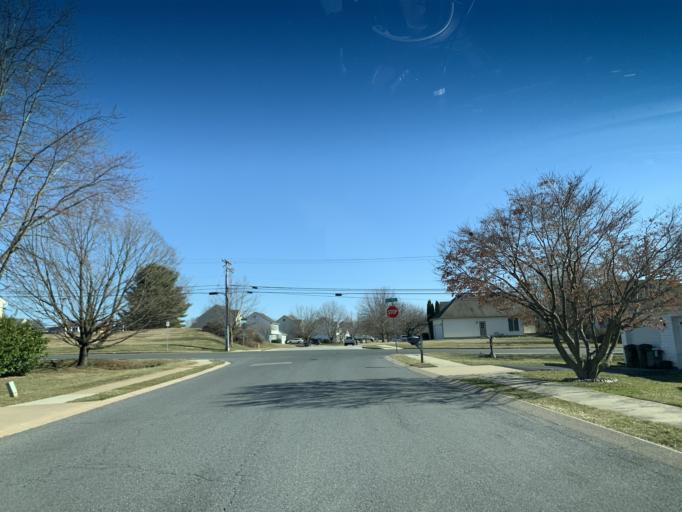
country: US
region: Maryland
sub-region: Carroll County
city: Westminster
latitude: 39.5941
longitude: -76.9903
